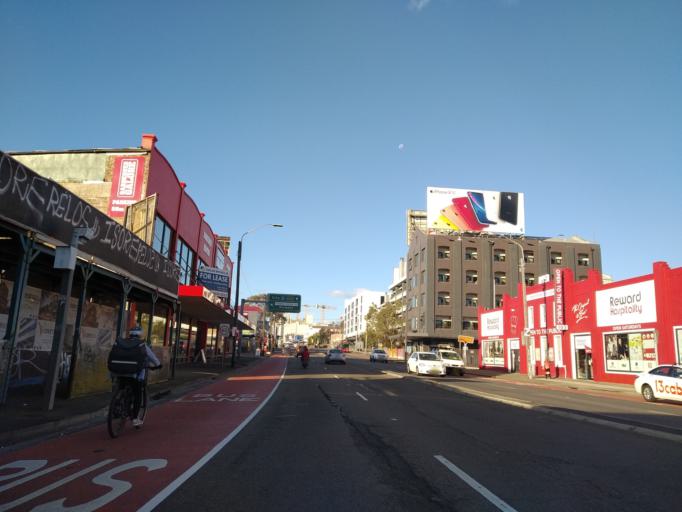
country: AU
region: New South Wales
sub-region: Marrickville
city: Camperdown
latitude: -33.8875
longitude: 151.1719
